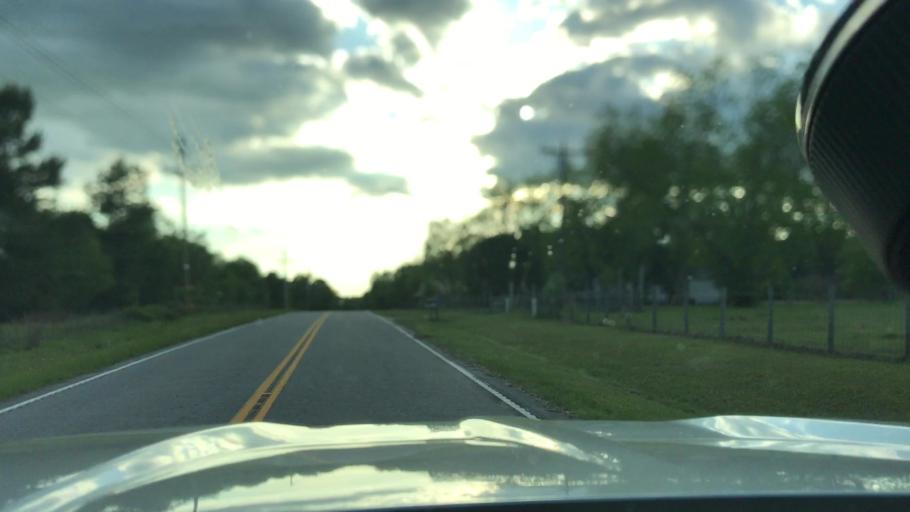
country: US
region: South Carolina
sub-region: Barnwell County
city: Blackville
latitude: 33.4736
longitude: -81.1963
